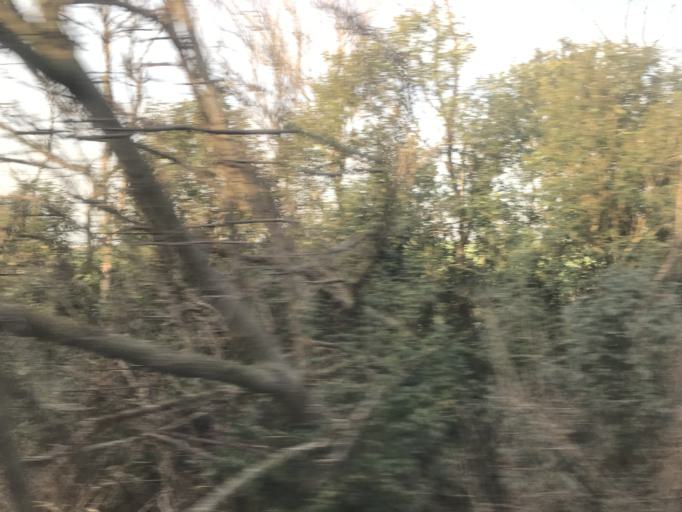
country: AR
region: Cordoba
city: Leones
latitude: -32.6815
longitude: -62.2057
